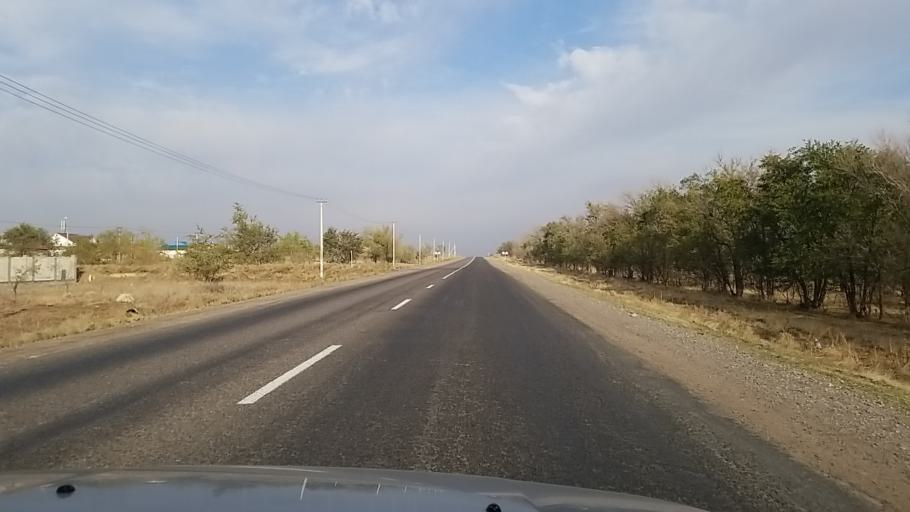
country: KZ
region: Almaty Oblysy
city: Burunday
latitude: 43.4829
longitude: 76.6751
